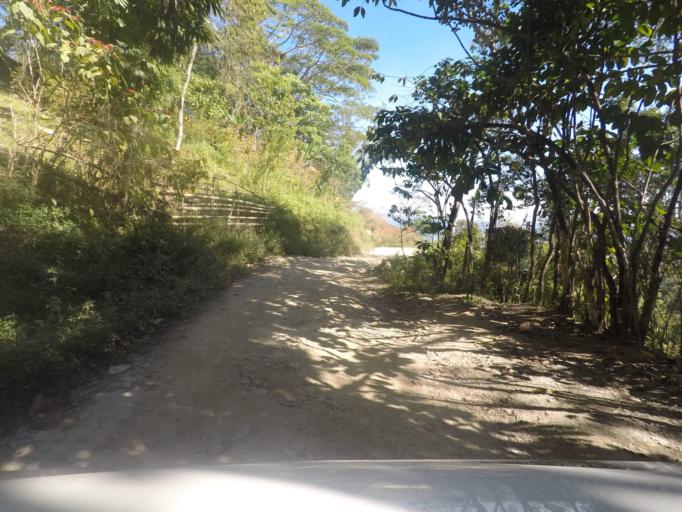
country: TL
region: Ermera
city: Gleno
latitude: -8.7310
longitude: 125.3418
